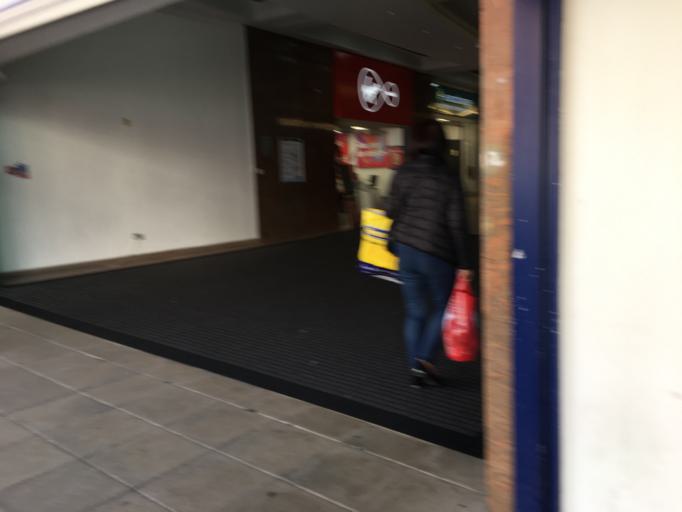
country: GB
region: England
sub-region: Walsall
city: Walsall
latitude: 52.5850
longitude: -1.9837
